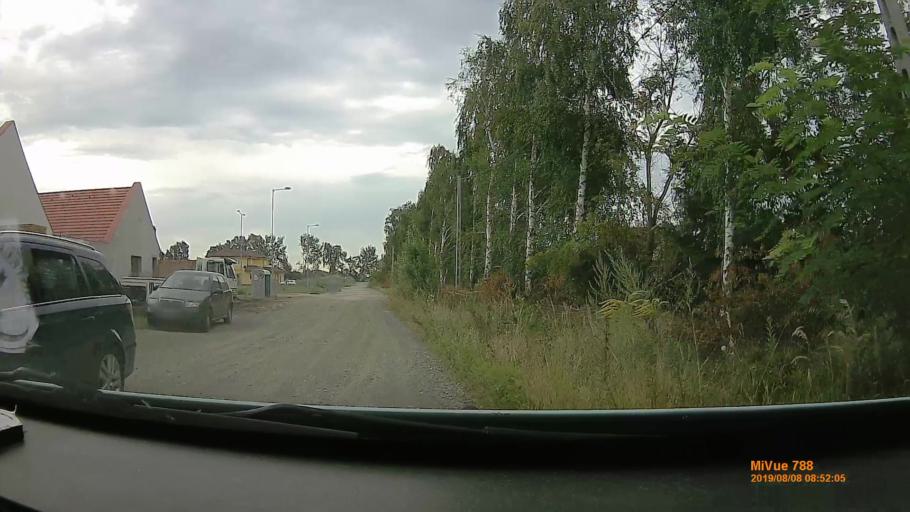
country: HU
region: Hajdu-Bihar
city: Debrecen
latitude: 47.6000
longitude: 21.6455
